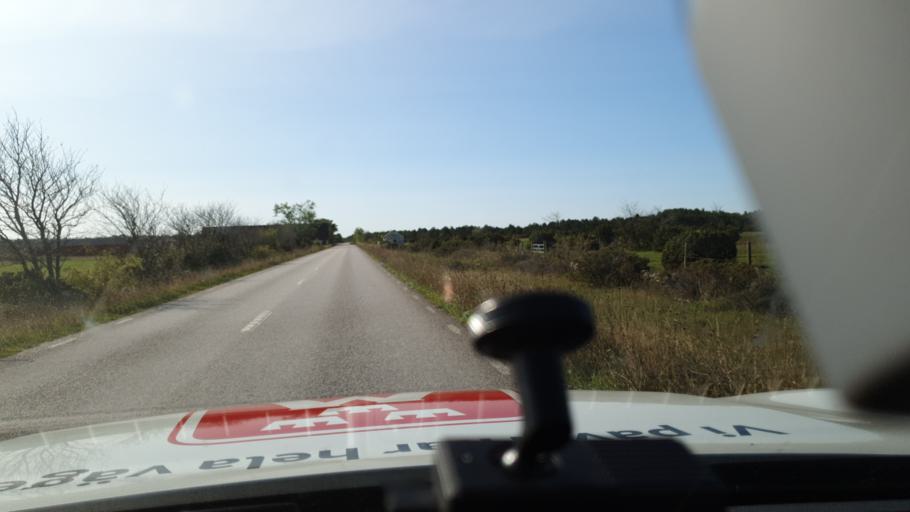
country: SE
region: Gotland
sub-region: Gotland
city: Hemse
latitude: 57.1316
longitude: 18.2803
